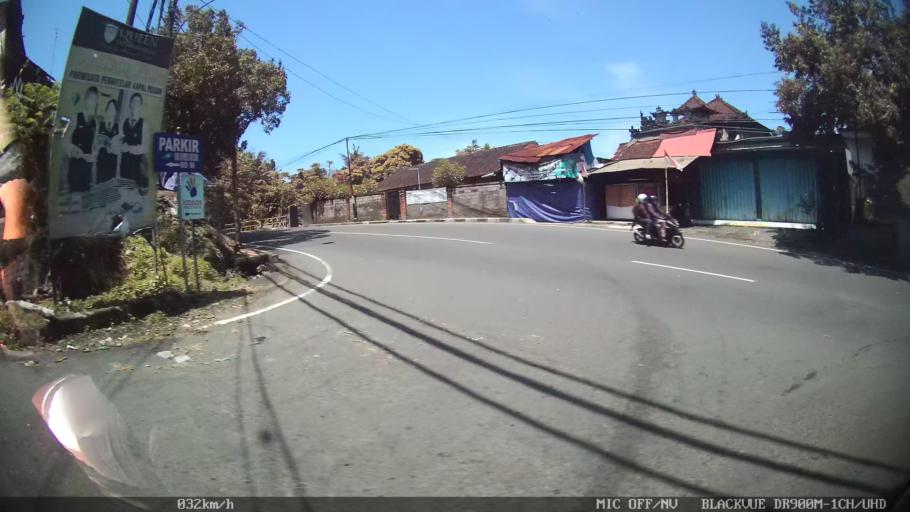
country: ID
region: Bali
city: Banjar Kelodan
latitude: -8.5410
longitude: 115.3349
